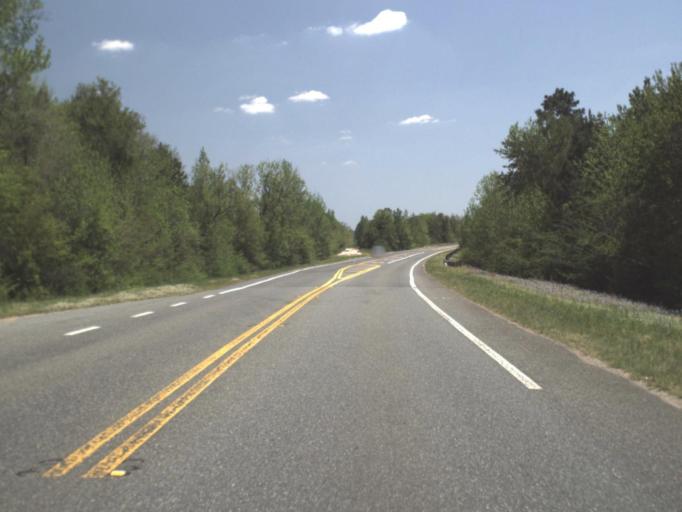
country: US
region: Florida
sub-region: Escambia County
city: Century
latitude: 30.9730
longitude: -87.2418
